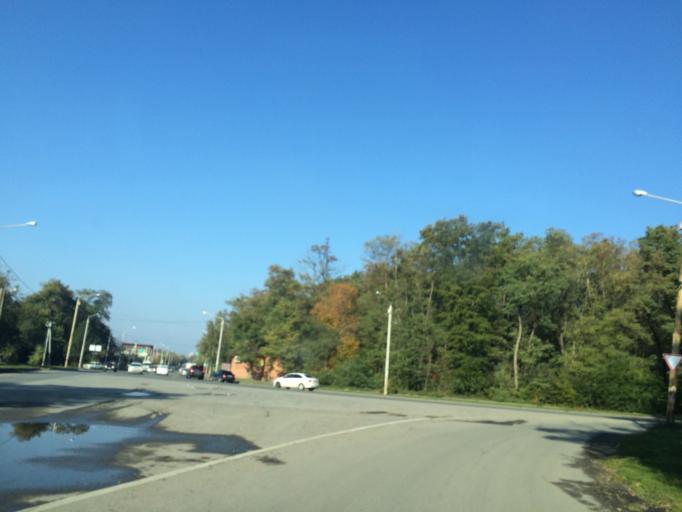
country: RU
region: Rostov
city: Imeni Chkalova
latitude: 47.2742
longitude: 39.7954
